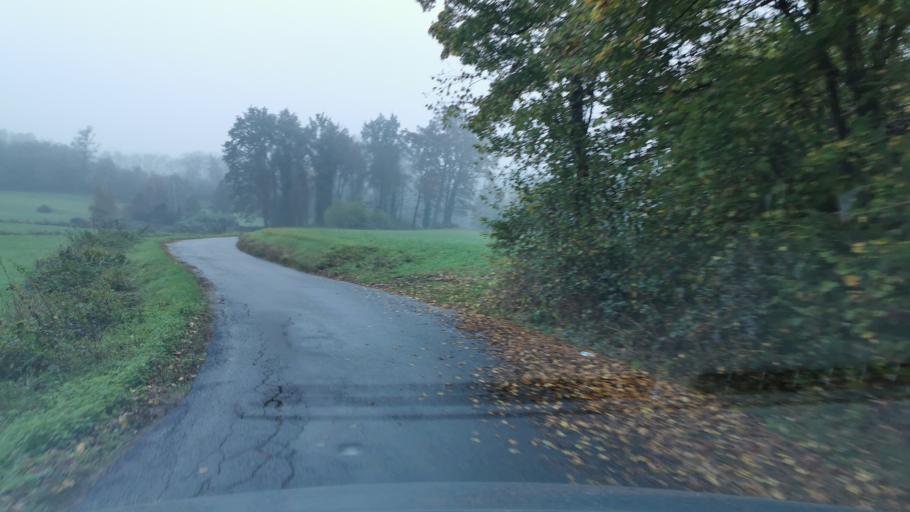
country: IT
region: Piedmont
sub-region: Provincia di Torino
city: Vialfre
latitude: 45.3757
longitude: 7.8144
